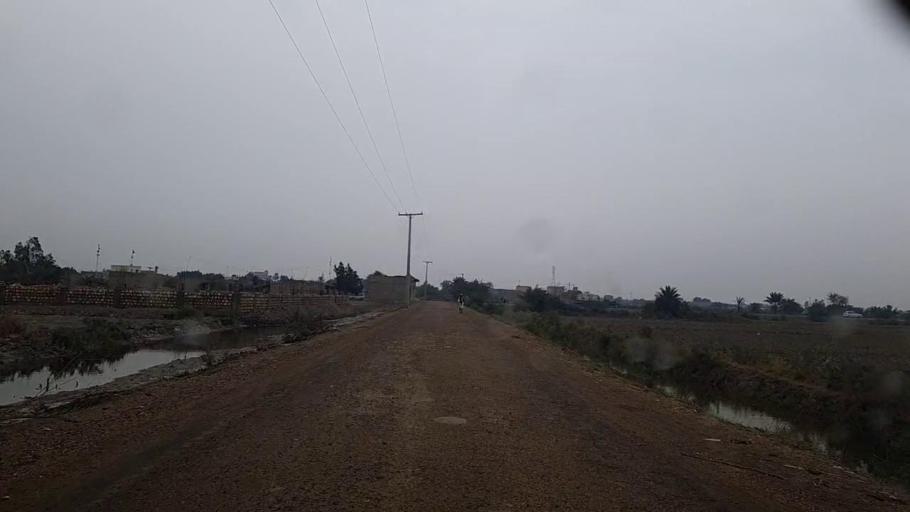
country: PK
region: Sindh
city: Ranipur
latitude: 27.2587
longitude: 68.5866
